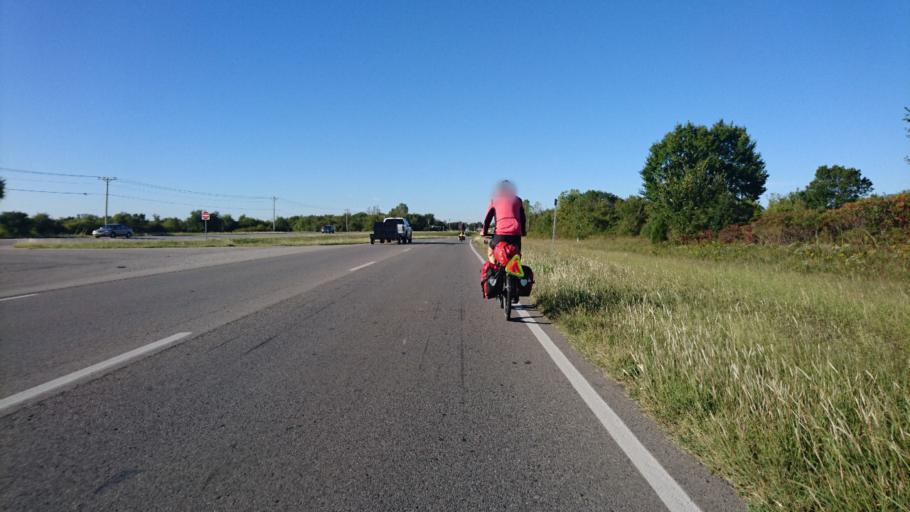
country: US
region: Oklahoma
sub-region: Rogers County
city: Claremore
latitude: 36.2724
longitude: -95.6444
